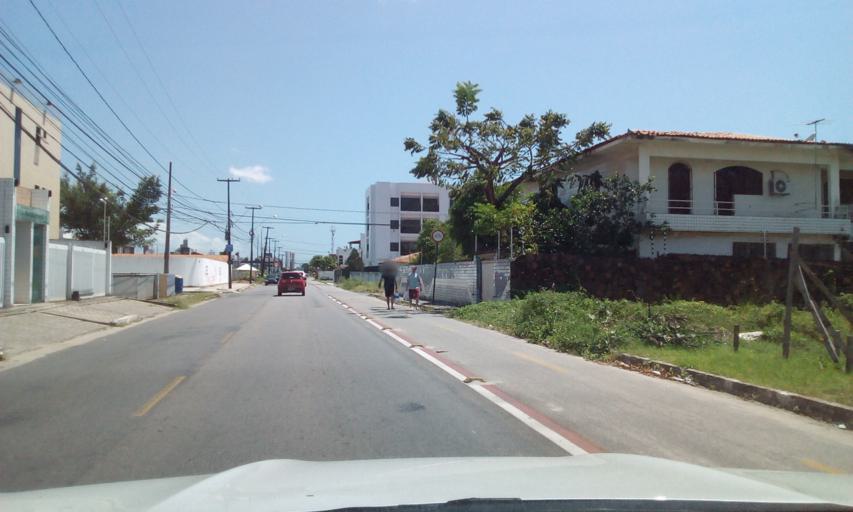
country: BR
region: Paraiba
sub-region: Joao Pessoa
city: Joao Pessoa
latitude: -7.0703
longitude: -34.8429
